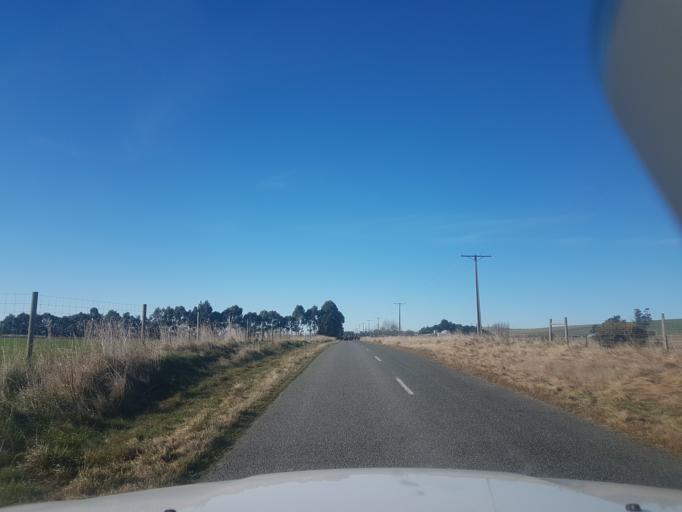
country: NZ
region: Canterbury
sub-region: Timaru District
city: Pleasant Point
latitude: -44.2913
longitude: 171.0608
